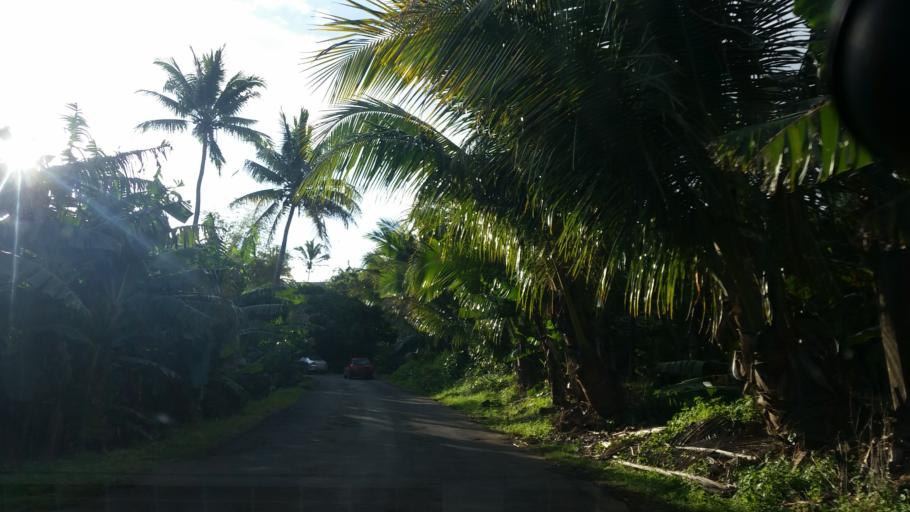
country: RE
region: Reunion
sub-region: Reunion
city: Saint-Joseph
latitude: -21.3768
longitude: 55.6697
